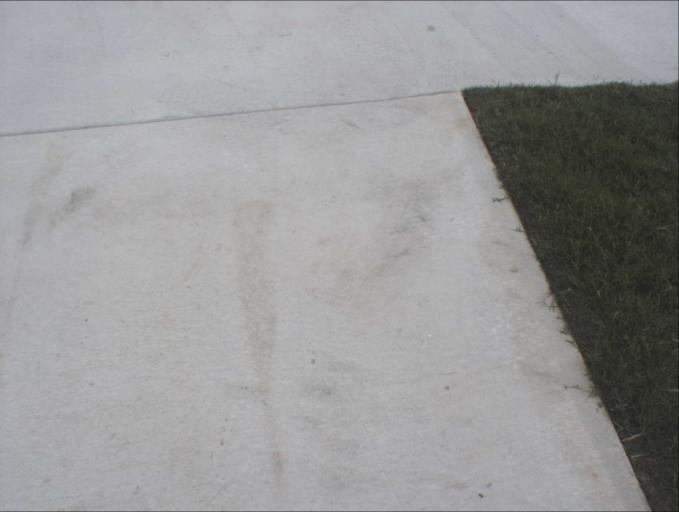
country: AU
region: Queensland
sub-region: Logan
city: Park Ridge South
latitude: -27.7062
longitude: 153.0388
